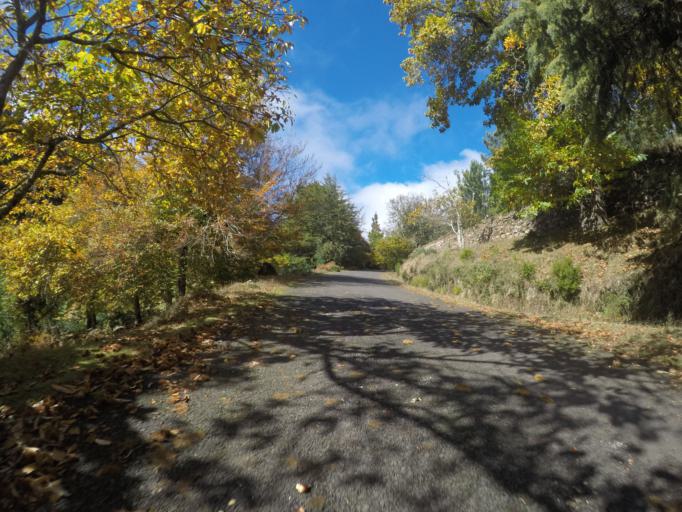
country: PT
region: Madeira
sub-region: Funchal
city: Nossa Senhora do Monte
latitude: 32.7023
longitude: -16.8873
